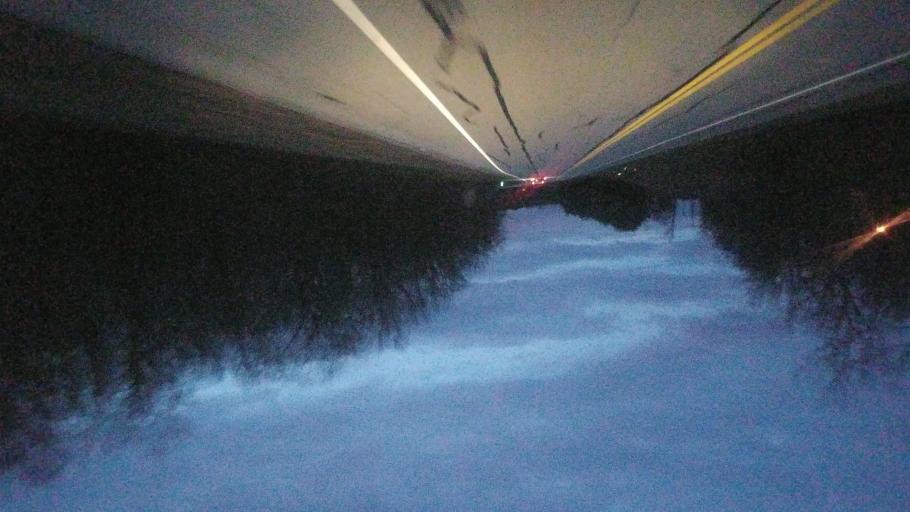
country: US
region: Tennessee
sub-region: Sequatchie County
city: Dunlap
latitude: 35.5010
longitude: -85.4737
